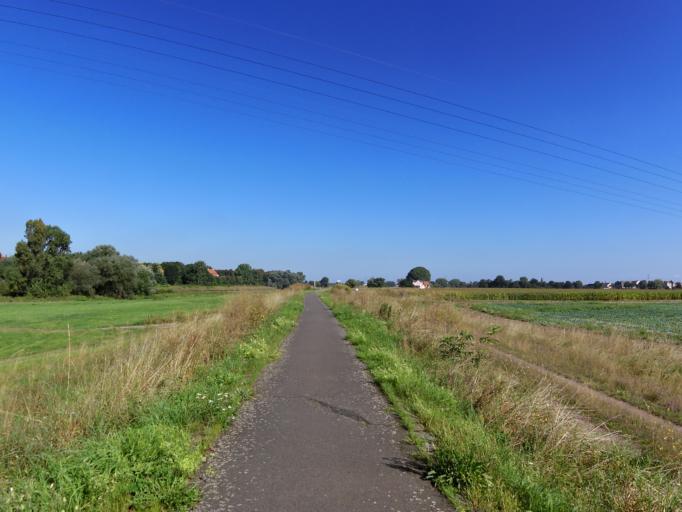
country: DE
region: Saxony
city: Riesa
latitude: 51.3147
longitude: 13.2944
